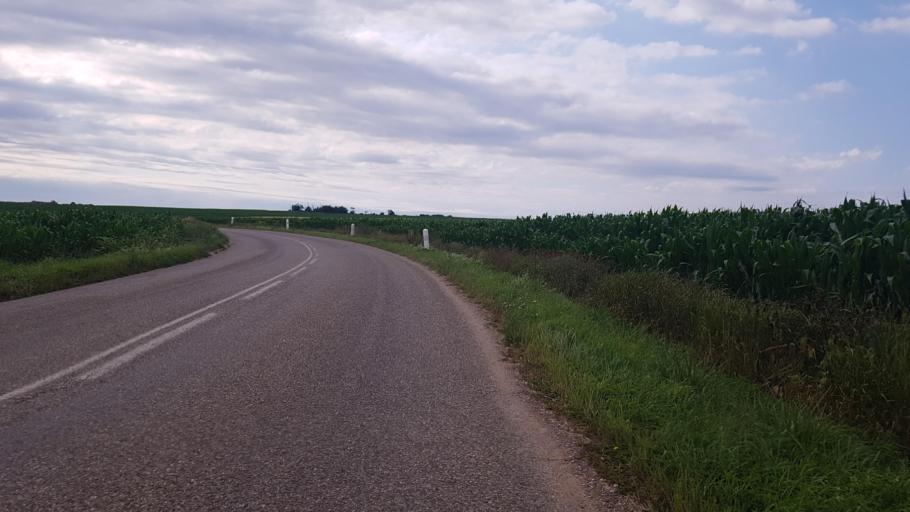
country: FR
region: Alsace
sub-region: Departement du Bas-Rhin
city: Hoerdt
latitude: 48.7215
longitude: 7.7766
